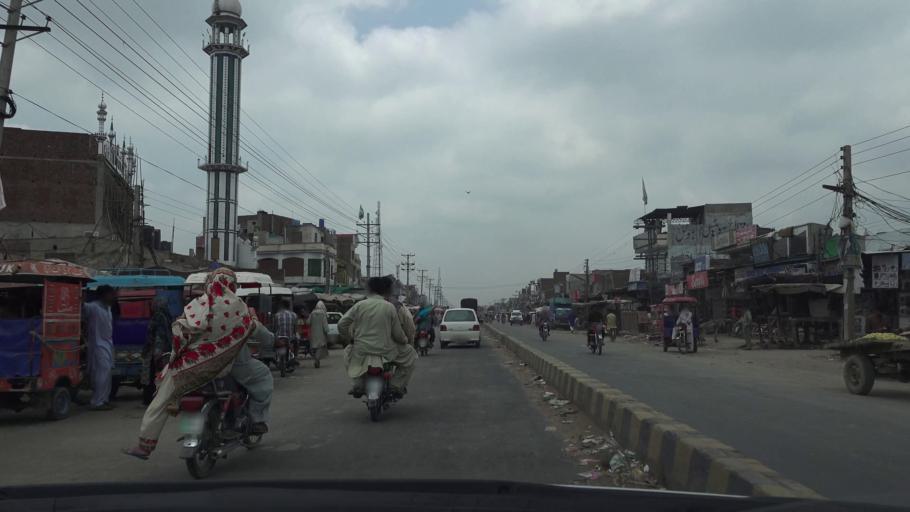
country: PK
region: Punjab
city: Faisalabad
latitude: 31.3889
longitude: 73.1956
